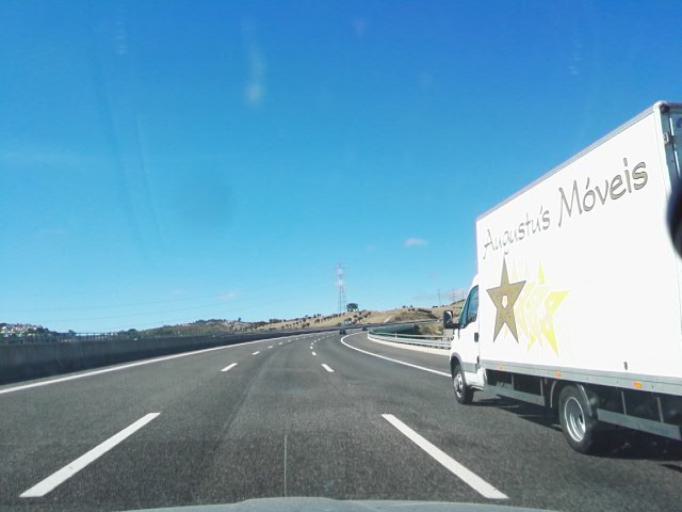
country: PT
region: Lisbon
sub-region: Vila Franca de Xira
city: Castanheira do Ribatejo
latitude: 38.9974
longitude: -9.0171
